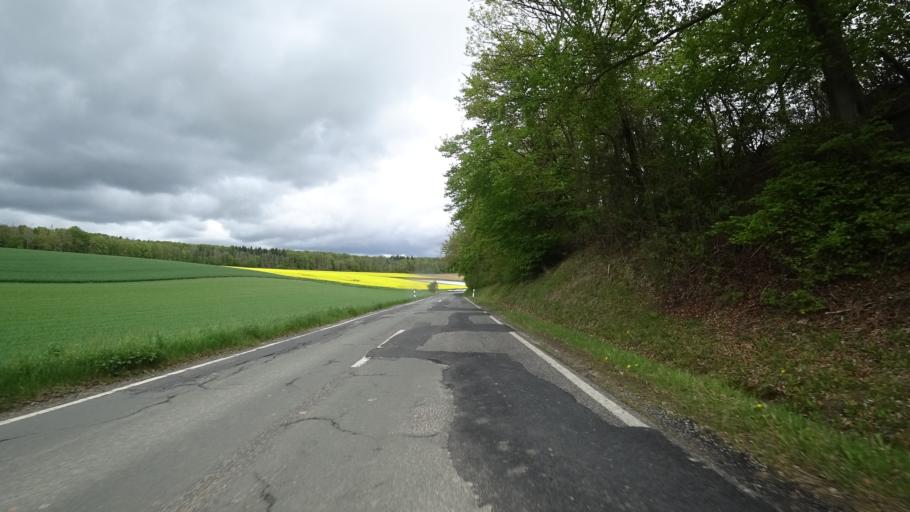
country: DE
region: Hesse
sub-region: Regierungsbezirk Kassel
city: Calden
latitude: 51.4408
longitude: 9.3595
